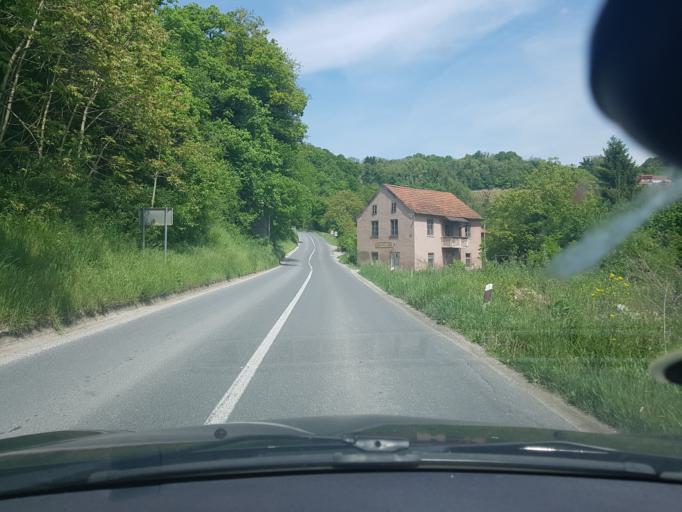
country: HR
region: Krapinsko-Zagorska
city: Pregrada
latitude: 46.1701
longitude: 15.7539
